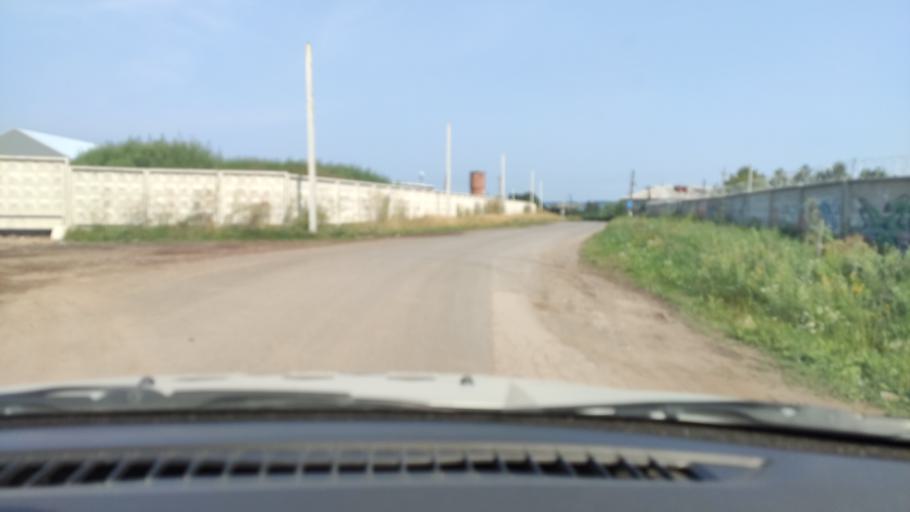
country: RU
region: Perm
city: Froly
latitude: 57.9065
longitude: 56.2030
